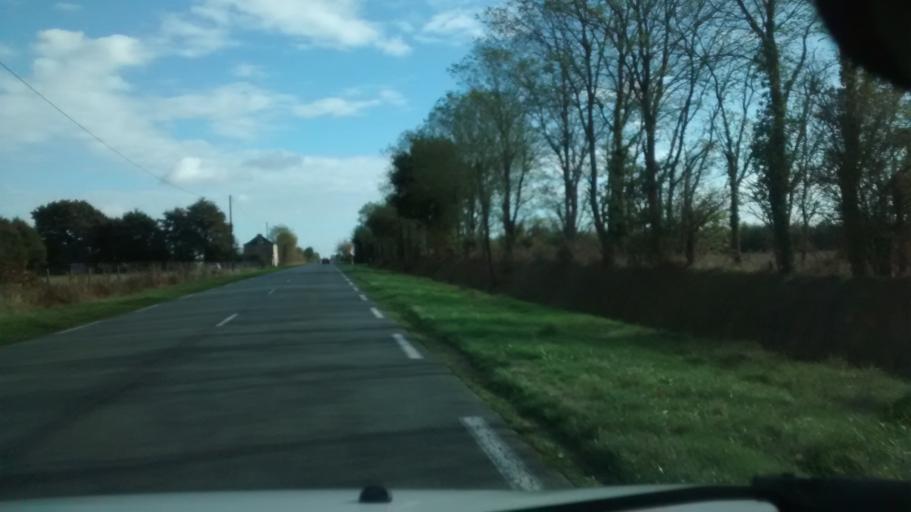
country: FR
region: Pays de la Loire
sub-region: Departement de Maine-et-Loire
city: Pouance
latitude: 47.7442
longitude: -1.2157
